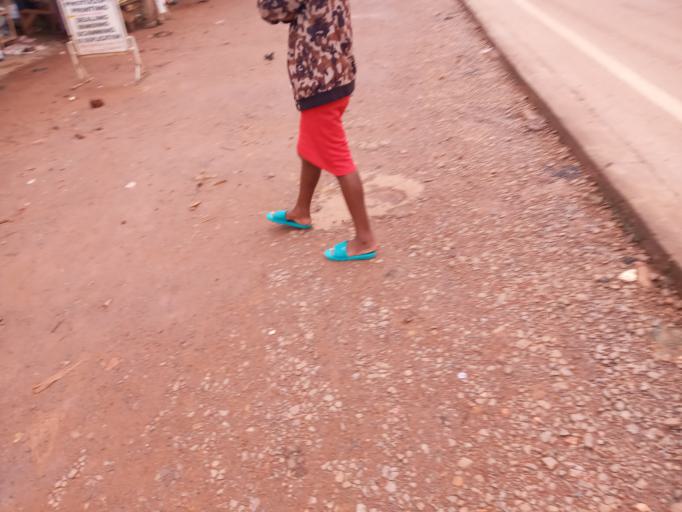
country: UG
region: Central Region
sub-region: Wakiso District
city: Bweyogerere
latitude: 0.3334
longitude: 32.6716
